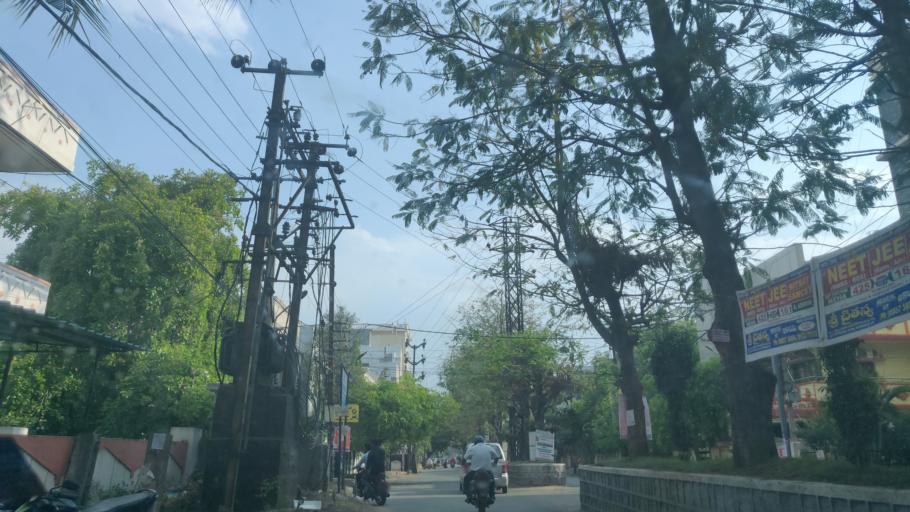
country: IN
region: Telangana
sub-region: Rangareddi
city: Gaddi Annaram
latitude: 17.3750
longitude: 78.5192
